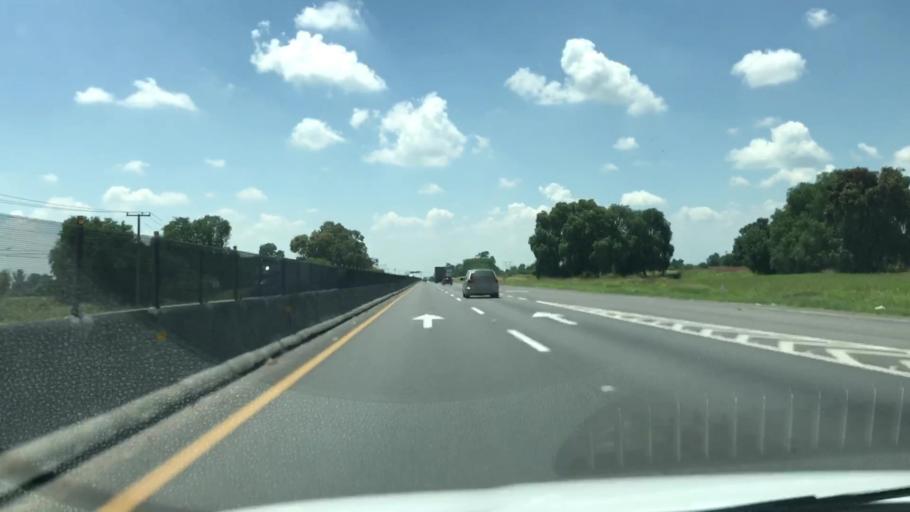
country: MX
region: Guanajuato
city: Villagran
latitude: 20.5122
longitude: -101.0132
